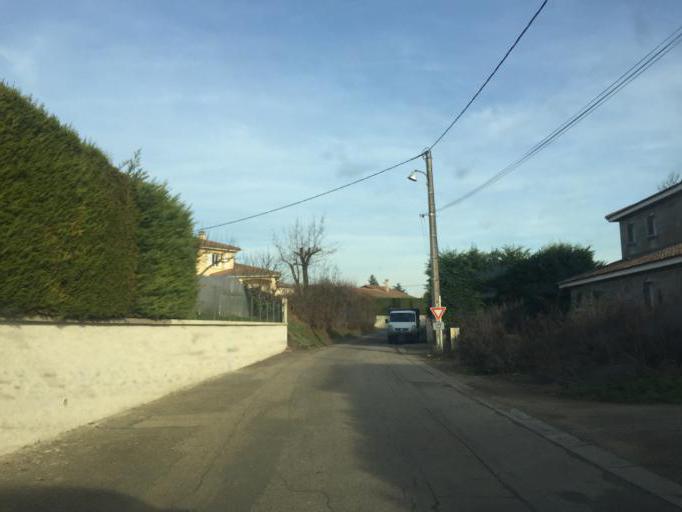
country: FR
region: Rhone-Alpes
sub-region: Departement de l'Ain
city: Miribel
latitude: 45.8309
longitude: 4.9508
